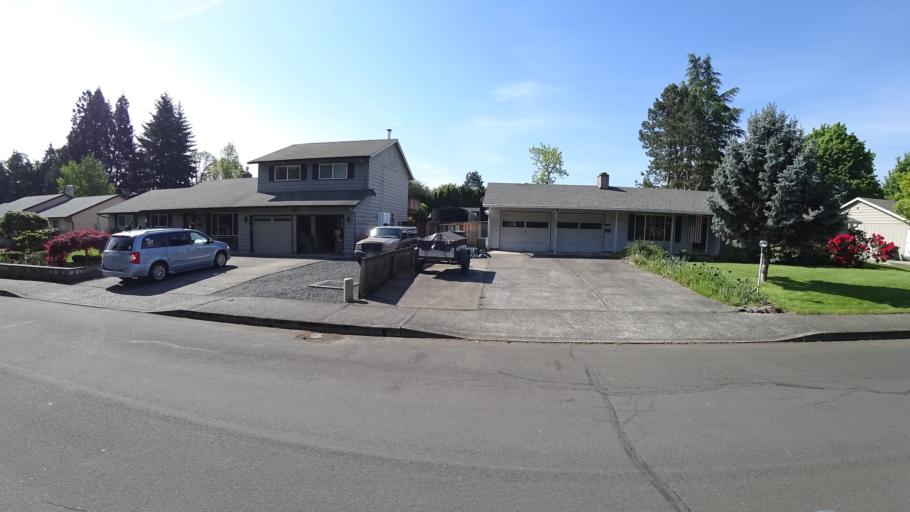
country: US
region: Oregon
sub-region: Washington County
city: Hillsboro
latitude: 45.5233
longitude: -122.9419
